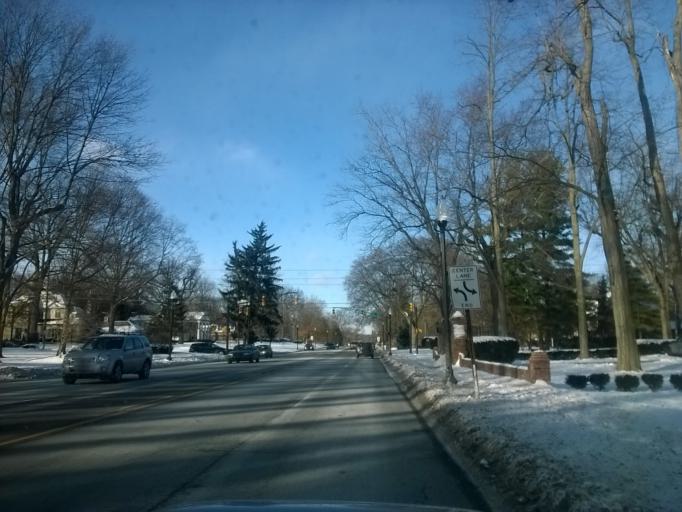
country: US
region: Indiana
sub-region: Marion County
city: Broad Ripple
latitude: 39.8535
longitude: -86.1571
